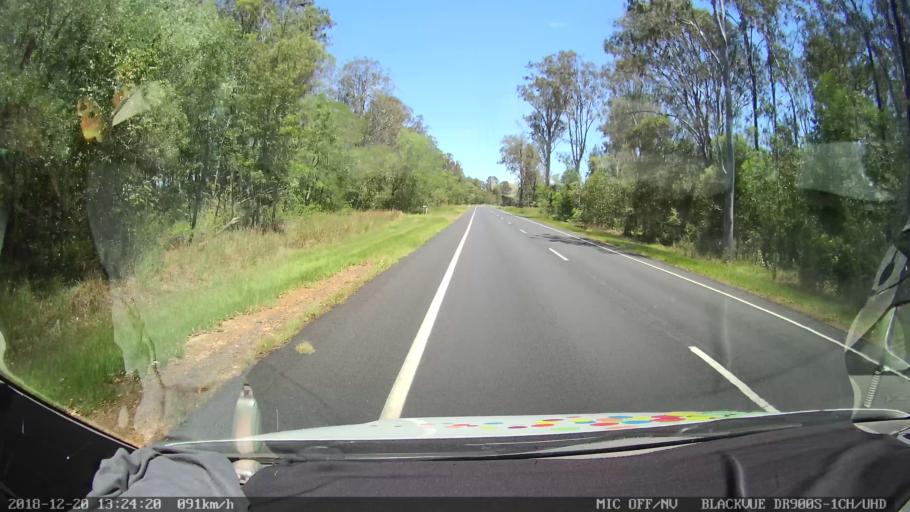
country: AU
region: New South Wales
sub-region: Richmond Valley
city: Casino
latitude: -29.1161
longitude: 153.0001
